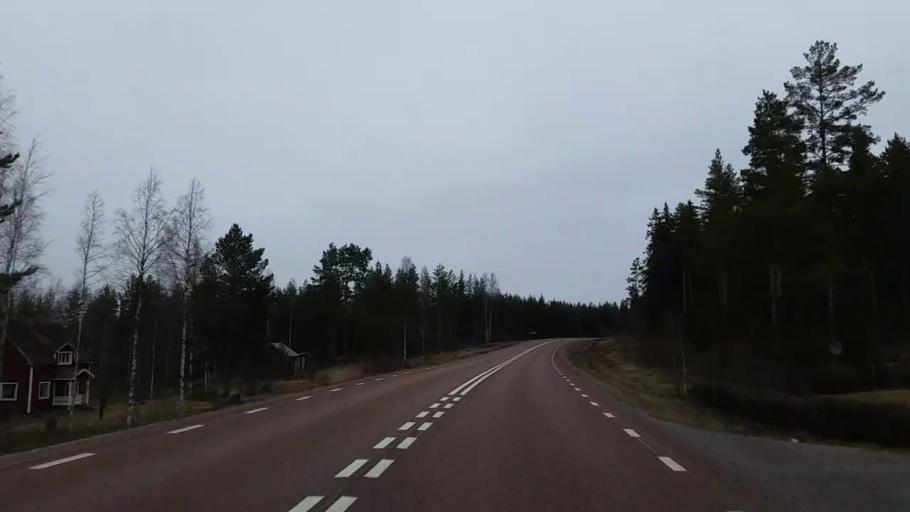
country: SE
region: Gaevleborg
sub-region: Ovanakers Kommun
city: Edsbyn
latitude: 61.2251
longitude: 15.8765
